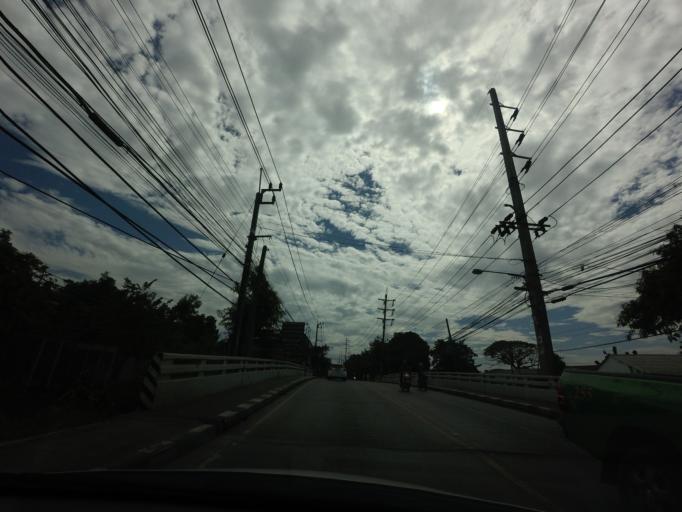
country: TH
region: Bangkok
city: Phra Khanong
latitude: 13.6739
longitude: 100.5911
